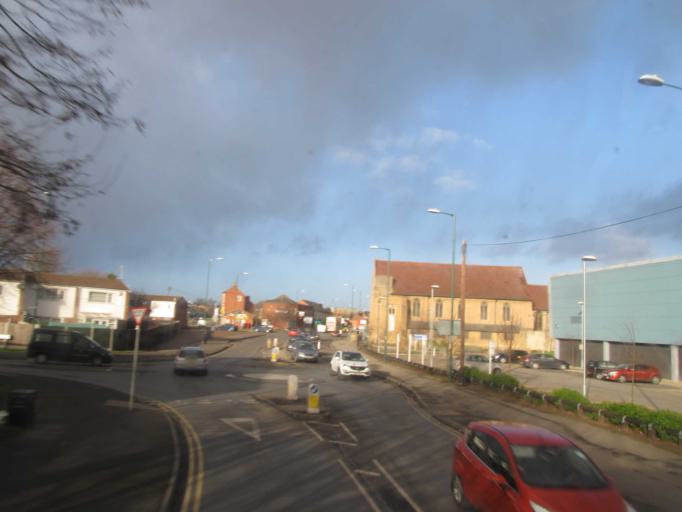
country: GB
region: England
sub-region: Nottinghamshire
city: Hucknall
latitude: 52.9964
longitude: -1.1972
